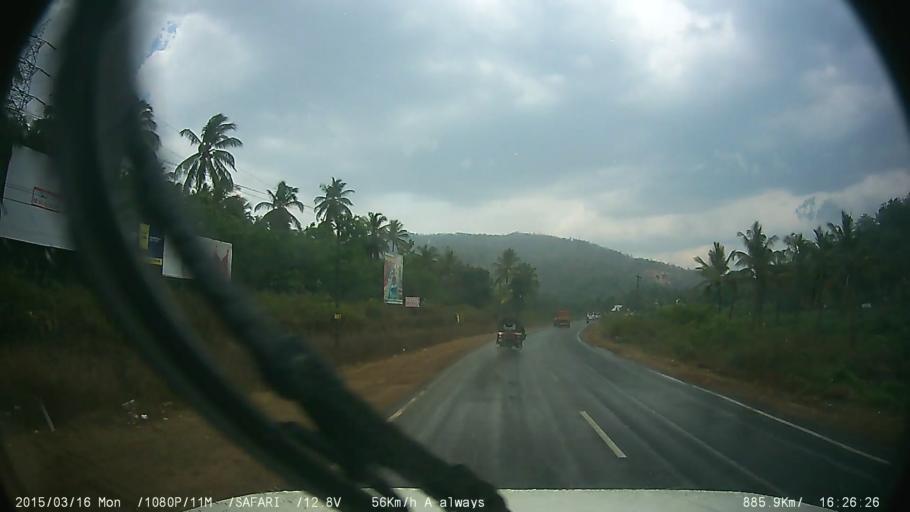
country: IN
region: Kerala
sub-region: Thrissur District
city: Chelakara
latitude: 10.5749
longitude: 76.3915
